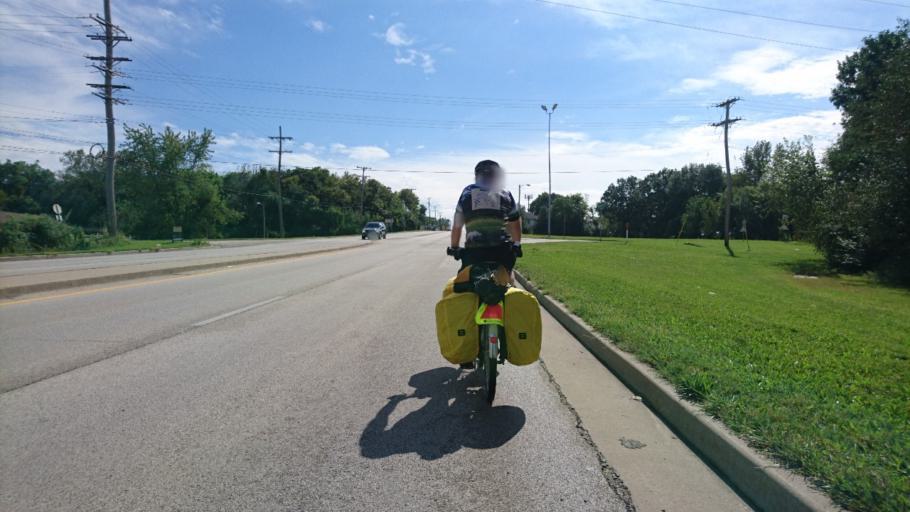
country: US
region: Illinois
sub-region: Sangamon County
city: Grandview
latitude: 39.8426
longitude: -89.6330
